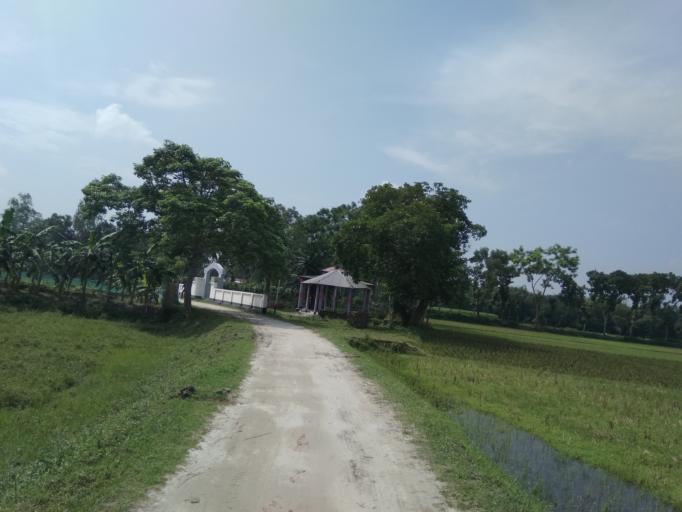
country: BD
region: Rangpur Division
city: Rangpur
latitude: 25.8385
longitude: 89.2039
